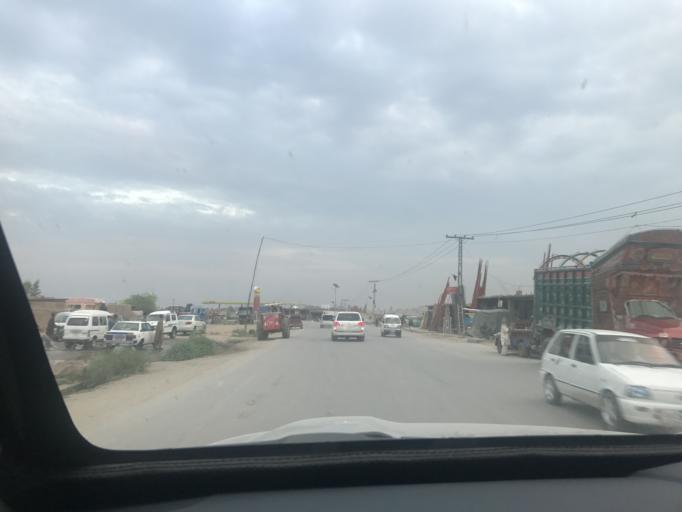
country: PK
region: Khyber Pakhtunkhwa
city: Peshawar
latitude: 33.9998
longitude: 71.3884
